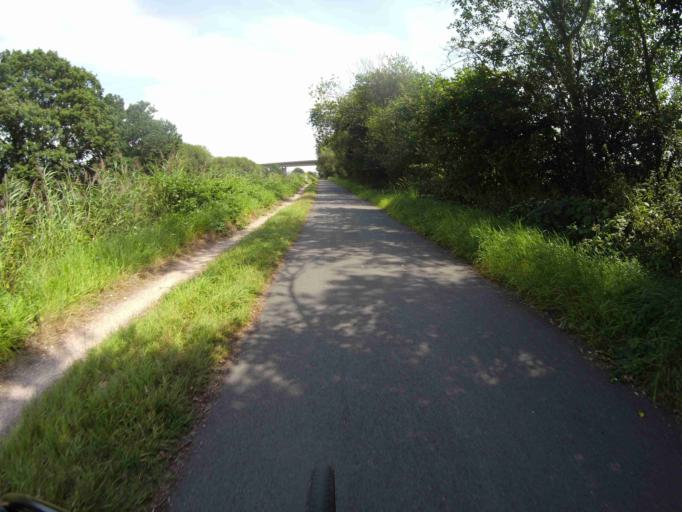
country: GB
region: England
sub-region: Devon
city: Exminster
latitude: 50.6887
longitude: -3.4864
